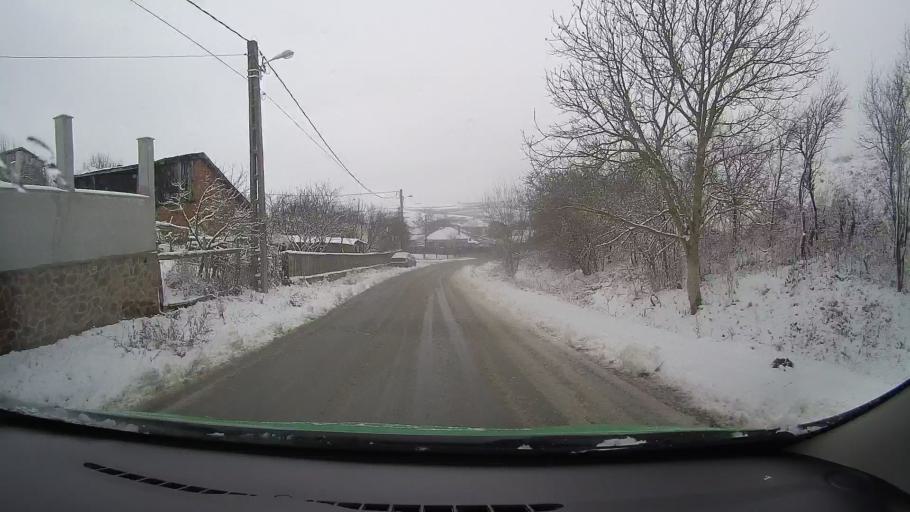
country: RO
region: Hunedoara
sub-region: Municipiul Hunedoara
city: Pestisu Mare
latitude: 45.8037
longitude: 22.9224
